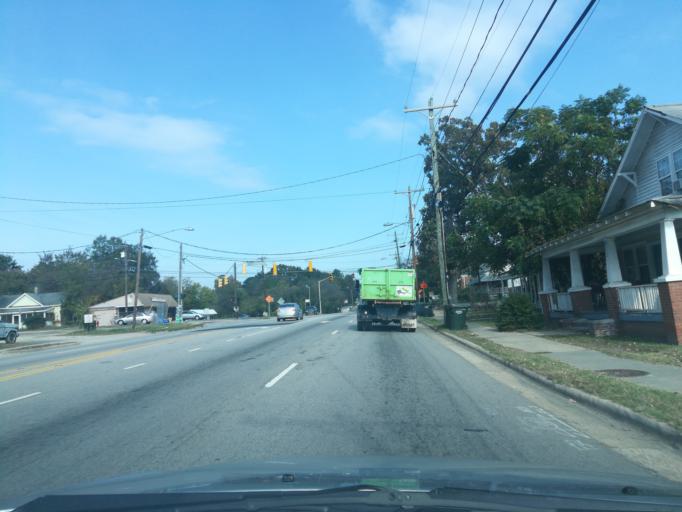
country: US
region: North Carolina
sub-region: Durham County
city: Durham
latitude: 35.9789
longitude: -78.8920
